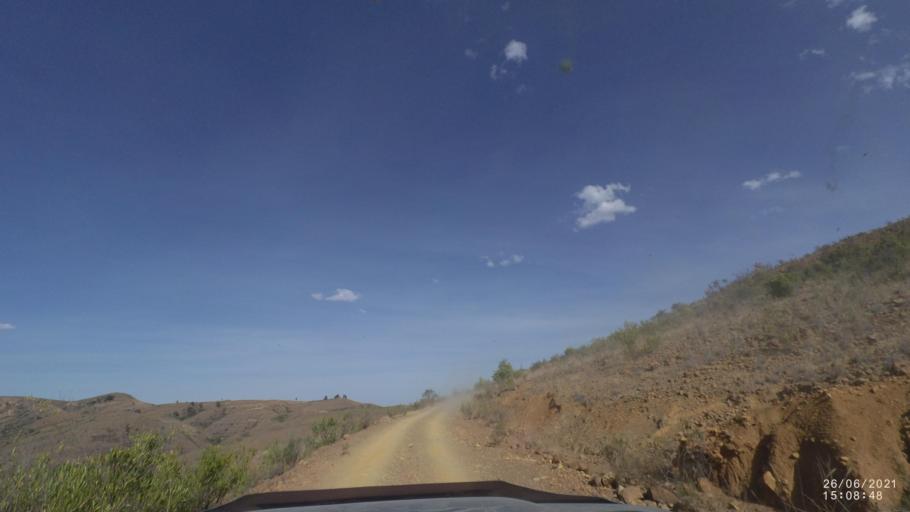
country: BO
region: Cochabamba
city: Mizque
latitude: -17.9492
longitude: -65.6395
